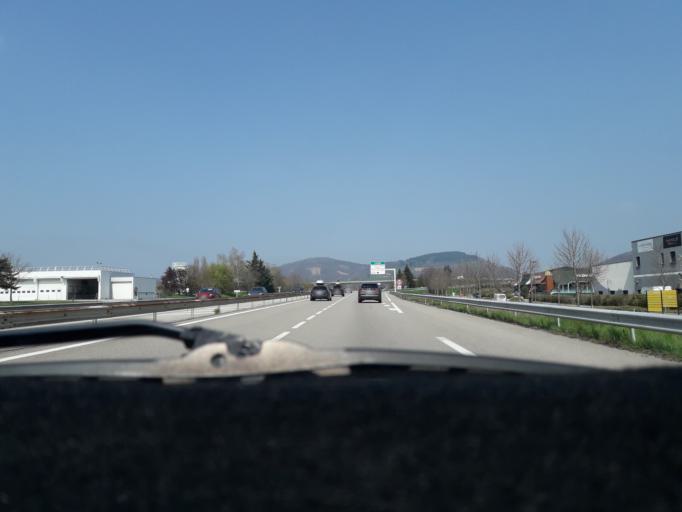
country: FR
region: Rhone-Alpes
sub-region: Departement de l'Isere
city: Apprieu
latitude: 45.3845
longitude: 5.4753
